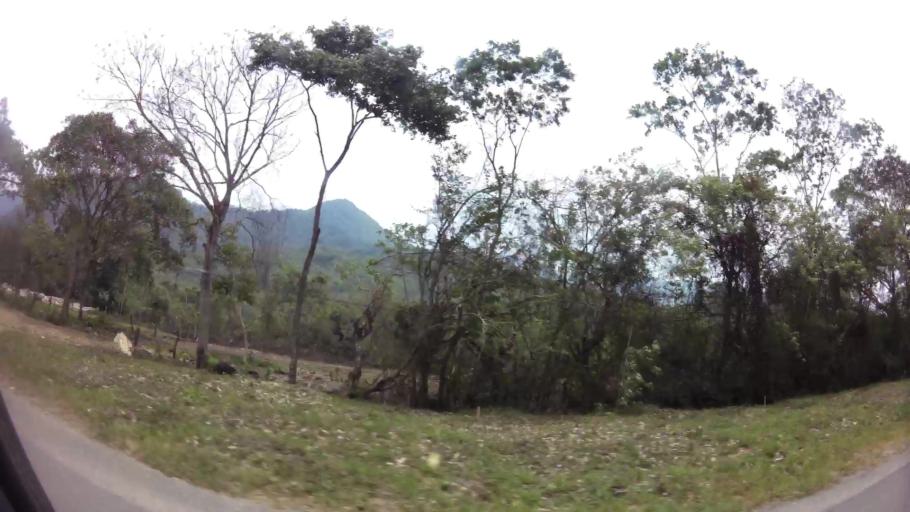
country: HN
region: Comayagua
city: Taulabe
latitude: 14.7219
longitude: -87.9646
